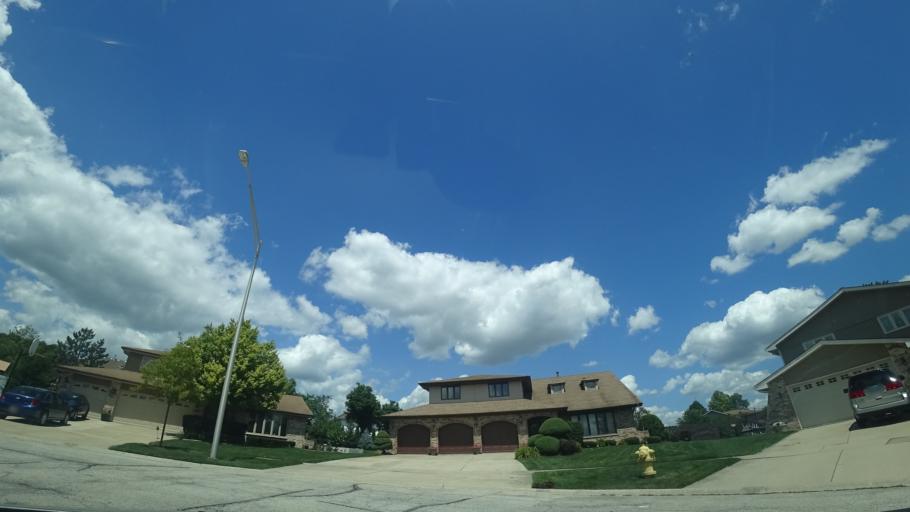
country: US
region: Illinois
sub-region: Will County
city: Homer Glen
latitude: 41.5783
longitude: -87.8968
